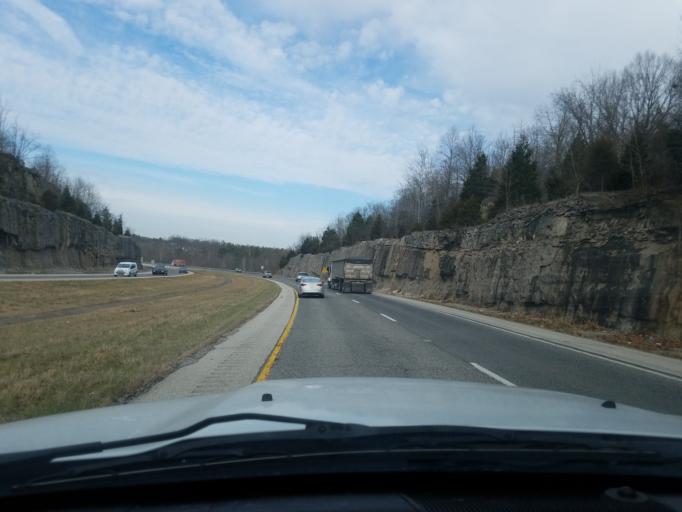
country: US
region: Indiana
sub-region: Lawrence County
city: Oolitic
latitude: 38.8769
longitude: -86.5188
